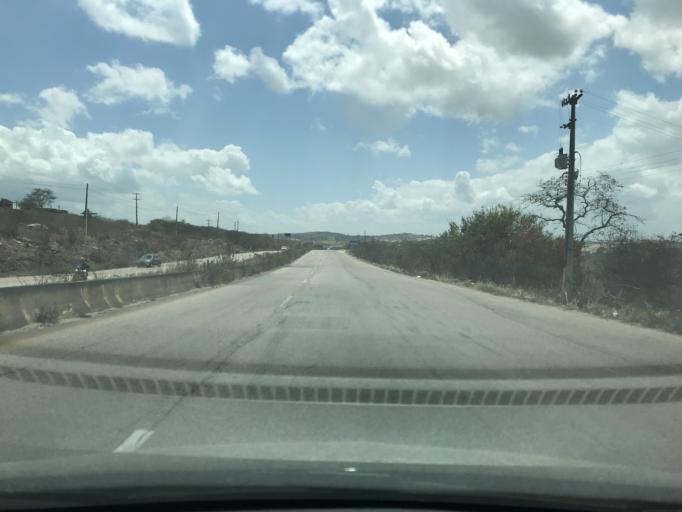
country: BR
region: Pernambuco
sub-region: Caruaru
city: Caruaru
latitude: -8.3076
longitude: -35.9438
